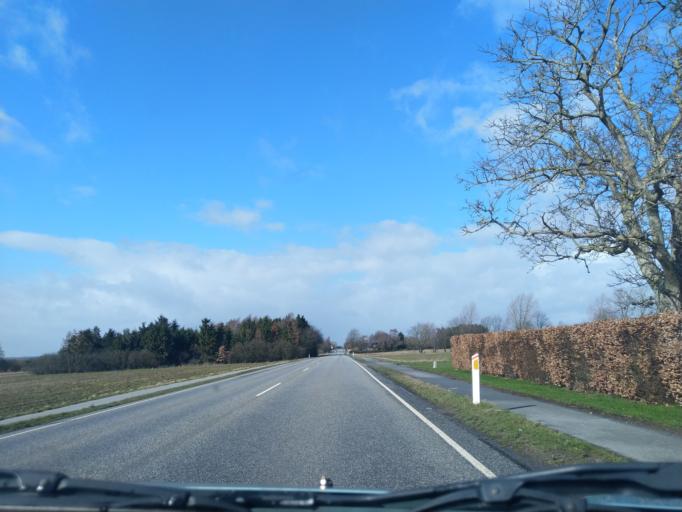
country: DK
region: Zealand
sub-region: Naestved Kommune
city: Naestved
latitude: 55.2824
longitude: 11.7157
